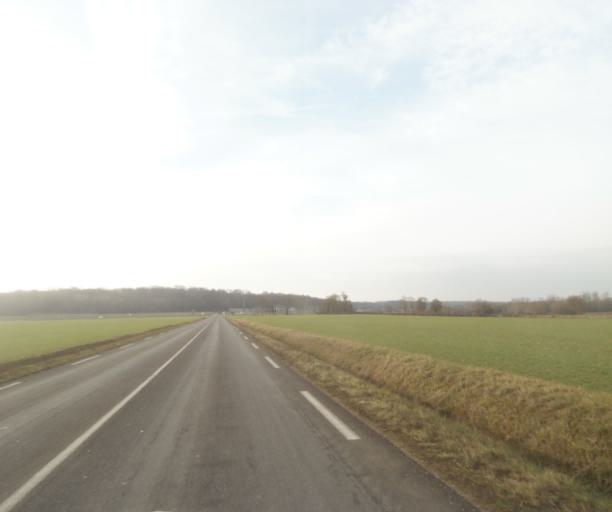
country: FR
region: Champagne-Ardenne
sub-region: Departement de la Haute-Marne
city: Saint-Dizier
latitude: 48.6245
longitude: 4.9303
